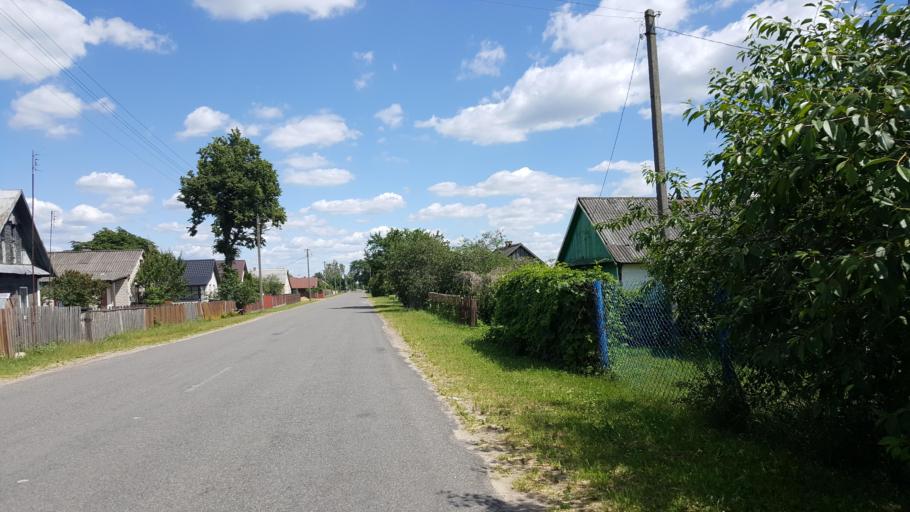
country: PL
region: Podlasie
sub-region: Powiat hajnowski
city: Czeremcha
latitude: 52.5385
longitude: 23.5436
